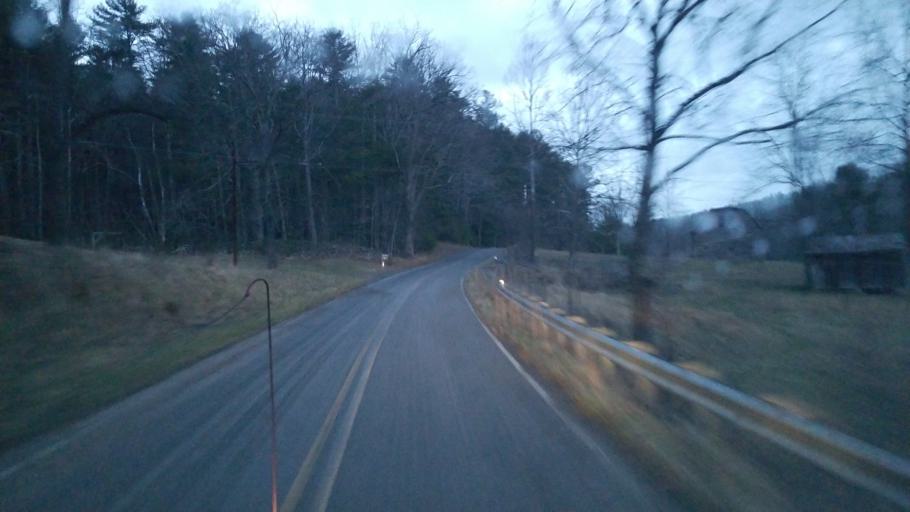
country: US
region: Virginia
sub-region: Pulaski County
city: Pulaski
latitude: 37.1203
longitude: -80.8722
